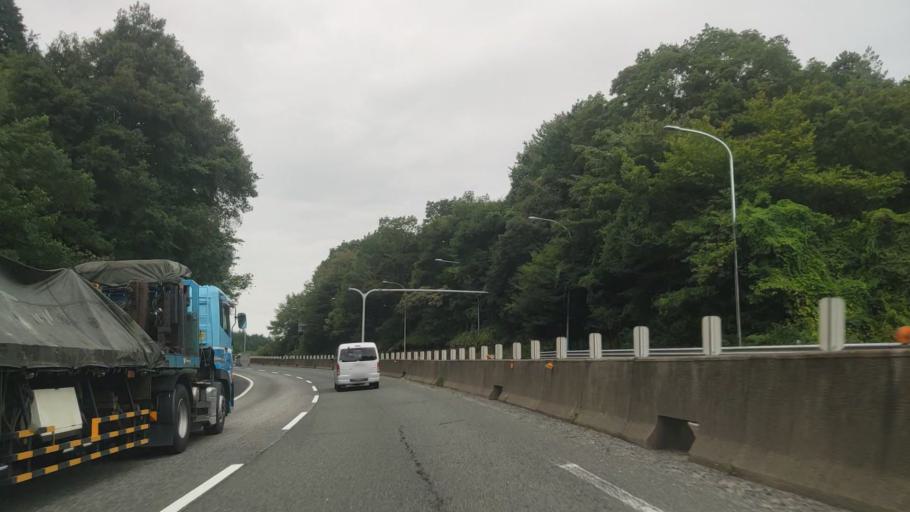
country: JP
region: Nara
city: Tenri
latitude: 34.6221
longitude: 135.8878
